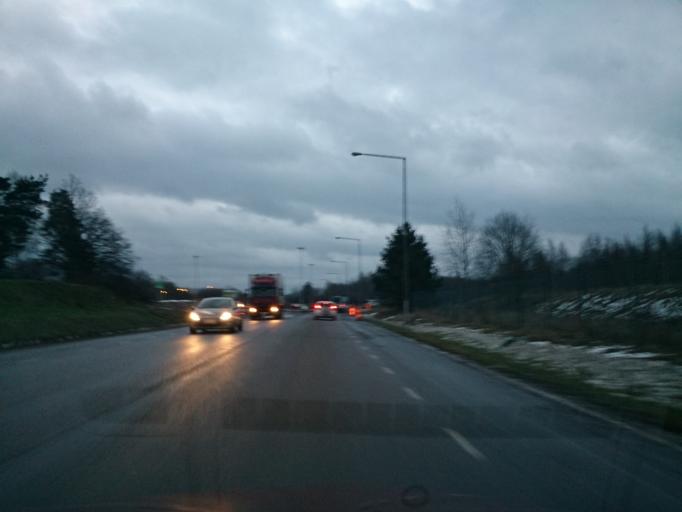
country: SE
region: OEstergoetland
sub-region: Linkopings Kommun
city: Linkoping
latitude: 58.3924
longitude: 15.6170
